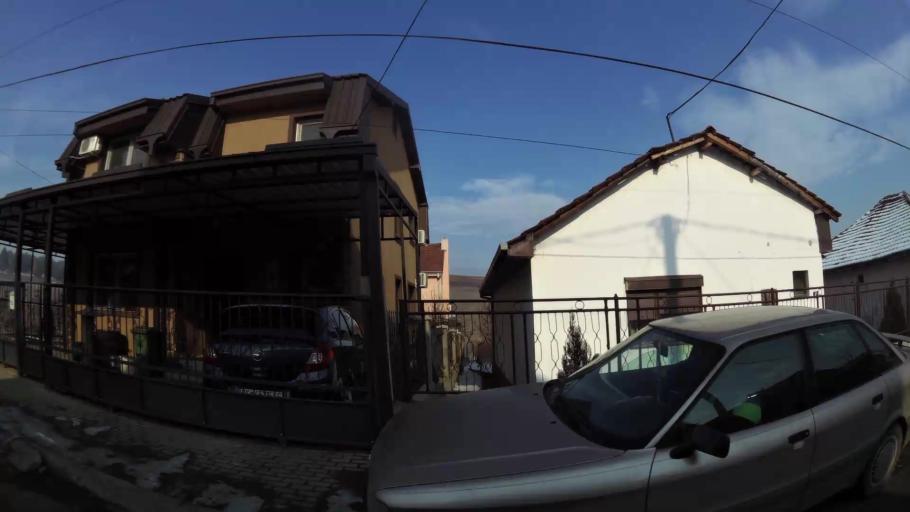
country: MK
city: Creshevo
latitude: 42.0126
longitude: 21.4959
